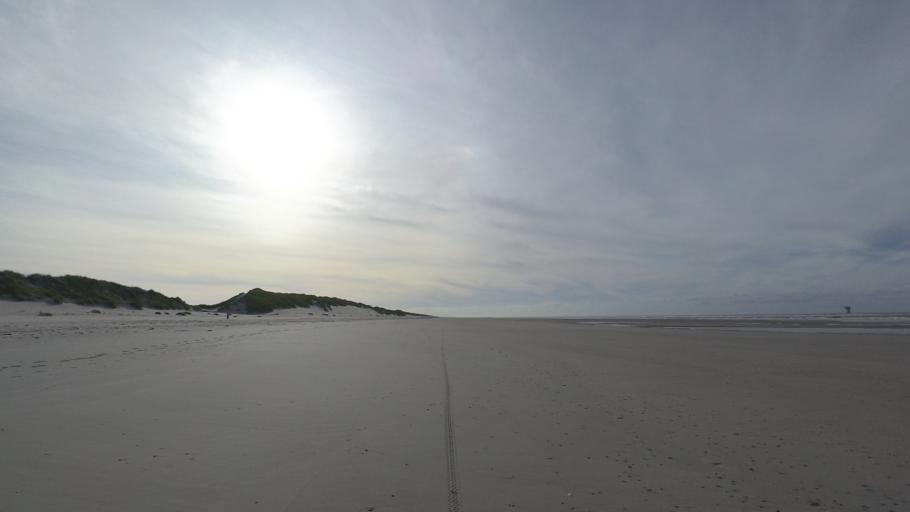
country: NL
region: Friesland
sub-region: Gemeente Dongeradeel
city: Holwerd
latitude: 53.4671
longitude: 5.8979
